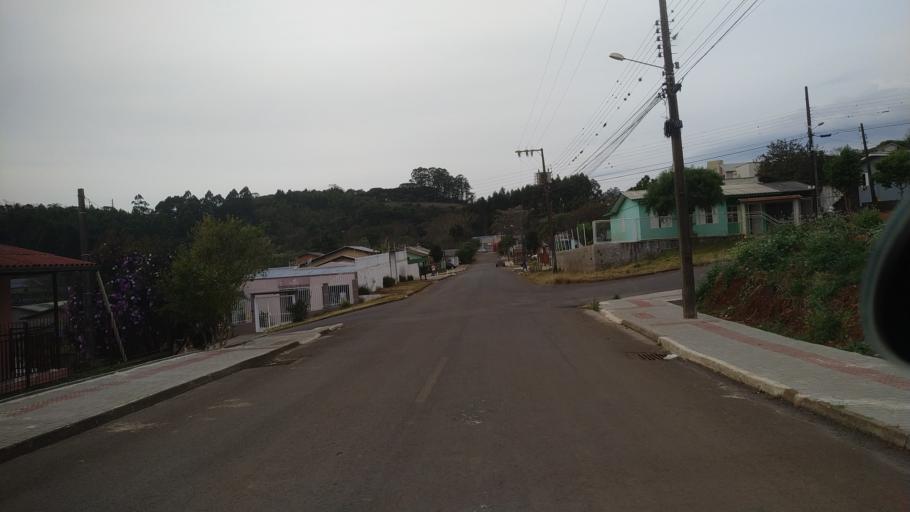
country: BR
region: Santa Catarina
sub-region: Chapeco
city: Chapeco
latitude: -27.1167
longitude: -52.5947
